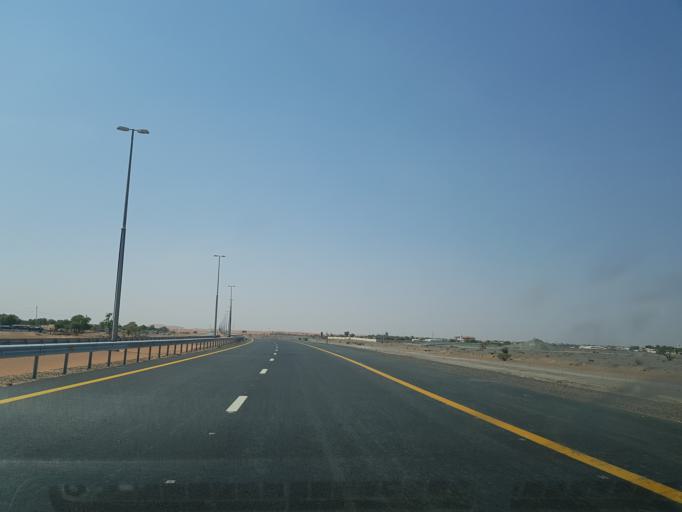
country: AE
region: Ash Shariqah
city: Adh Dhayd
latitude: 25.2353
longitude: 55.9050
